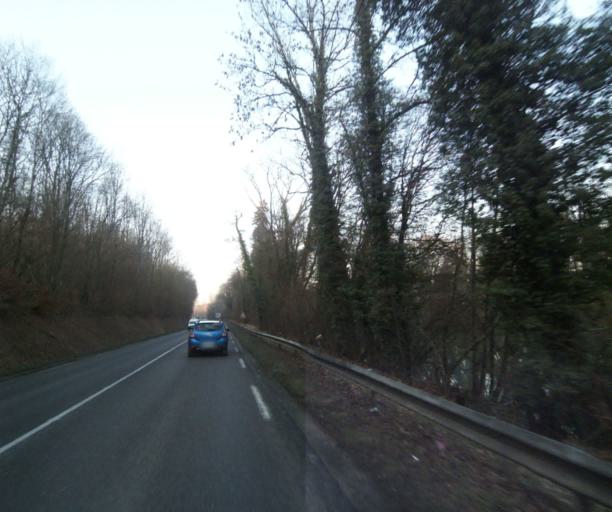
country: FR
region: Lorraine
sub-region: Departement de la Meuse
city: Ancerville
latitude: 48.6193
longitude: 4.9953
